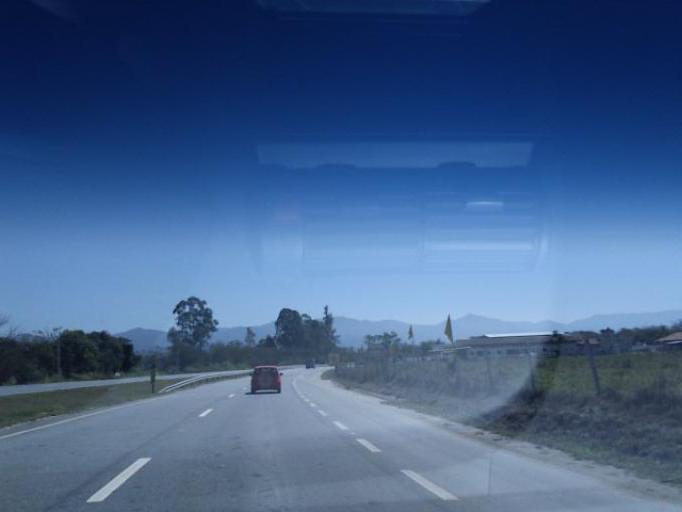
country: BR
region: Sao Paulo
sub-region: Taubate
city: Taubate
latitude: -23.0156
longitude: -45.6406
